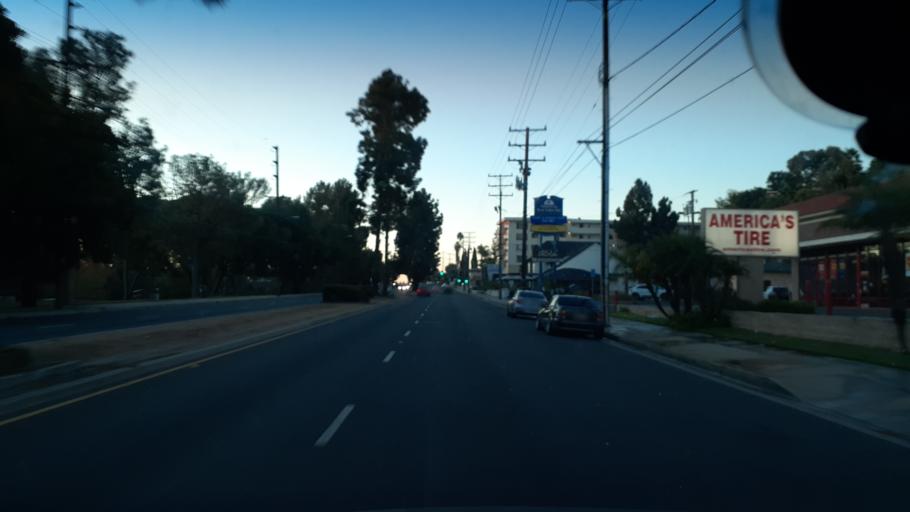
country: US
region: California
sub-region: Los Angeles County
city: San Pedro
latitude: 33.7494
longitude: -118.3094
